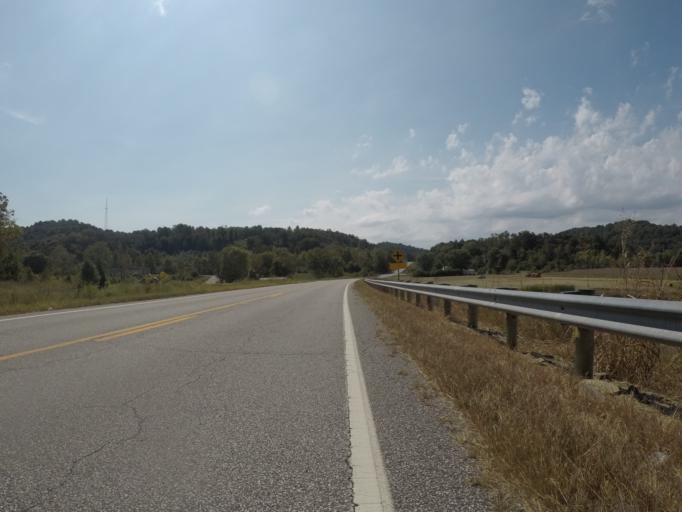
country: US
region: West Virginia
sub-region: Cabell County
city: Lesage
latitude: 38.5102
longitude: -82.3921
